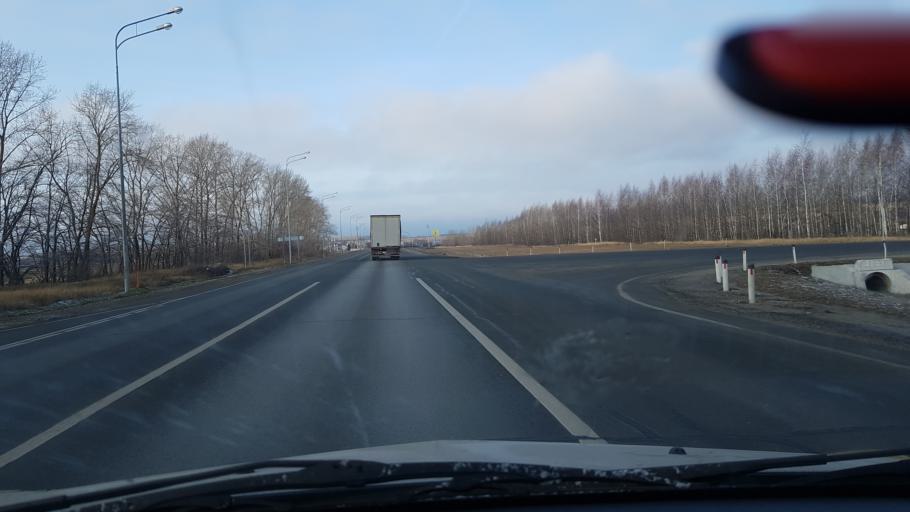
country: RU
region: Tatarstan
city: Laishevo
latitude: 55.3907
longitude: 49.8123
